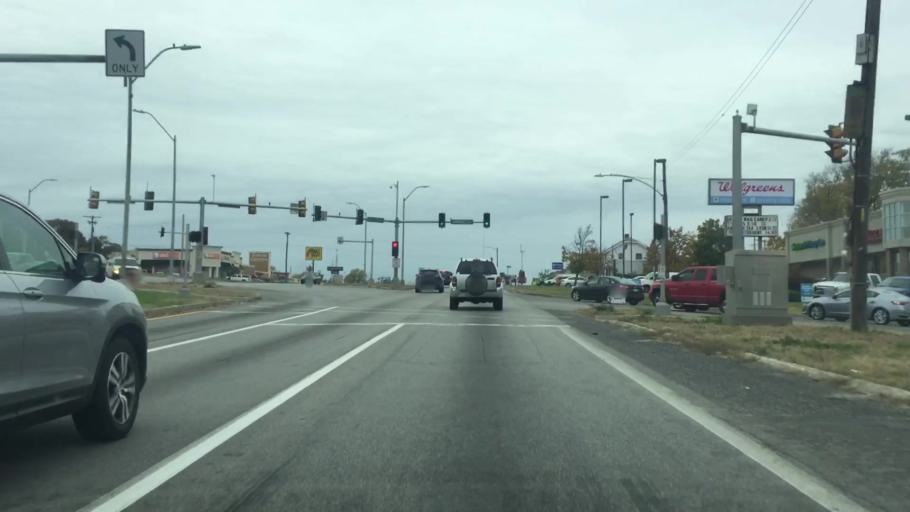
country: US
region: Missouri
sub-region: Jackson County
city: Raytown
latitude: 38.9944
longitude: -94.4730
